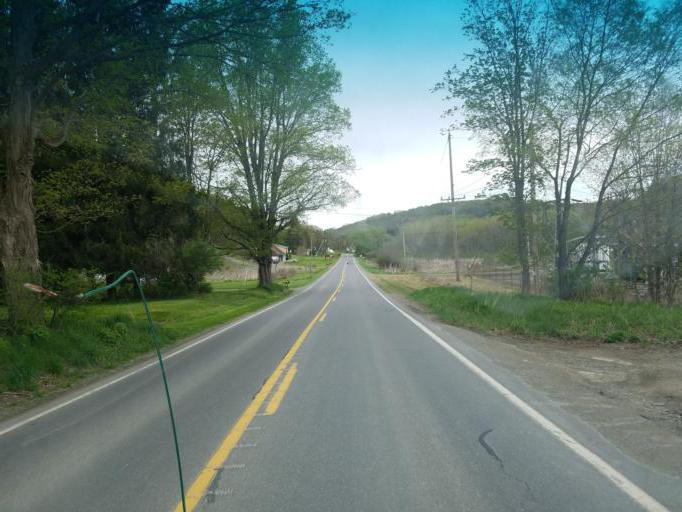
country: US
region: Pennsylvania
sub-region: Tioga County
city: Westfield
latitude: 41.8651
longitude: -77.5366
